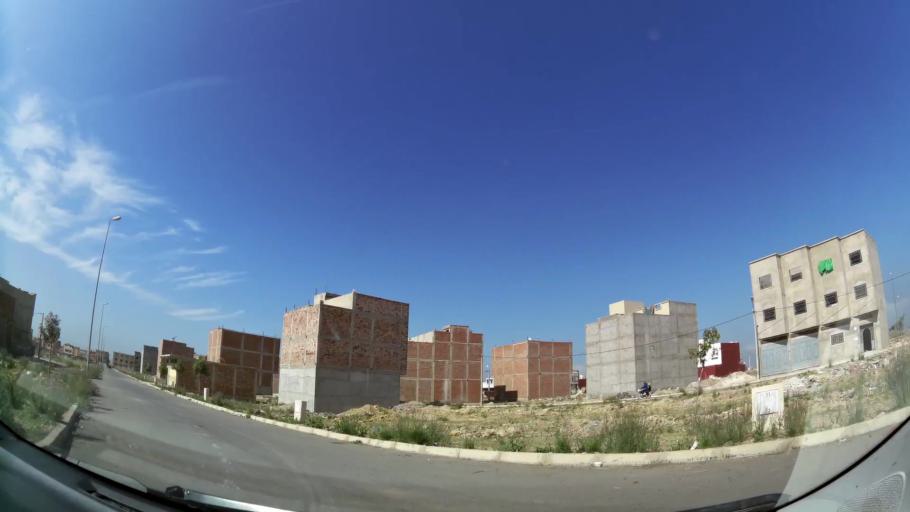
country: MA
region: Oriental
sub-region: Oujda-Angad
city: Oujda
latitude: 34.6958
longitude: -1.8704
